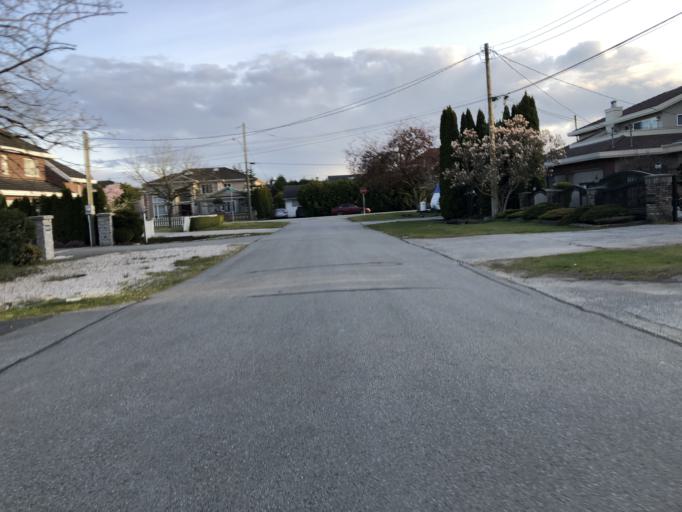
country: CA
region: British Columbia
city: Richmond
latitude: 49.1500
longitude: -123.1337
